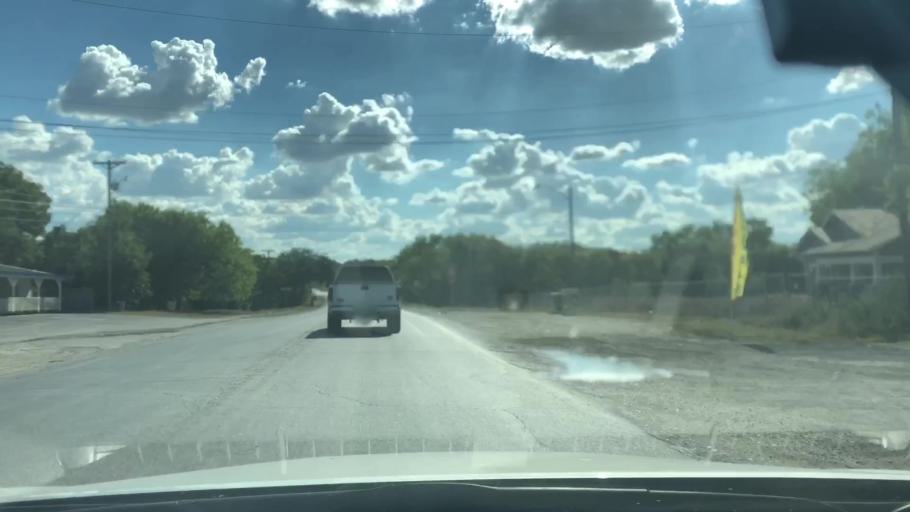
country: US
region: Texas
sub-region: Comal County
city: New Braunfels
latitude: 29.6659
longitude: -98.1714
